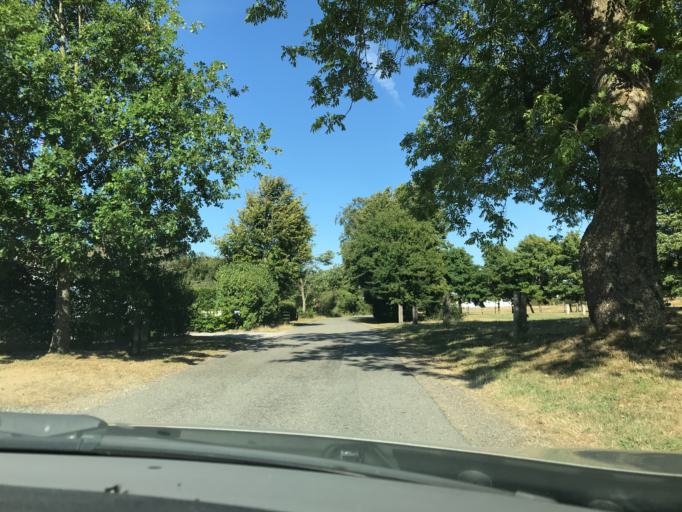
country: DK
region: South Denmark
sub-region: Kolding Kommune
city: Kolding
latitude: 55.5429
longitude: 9.4858
